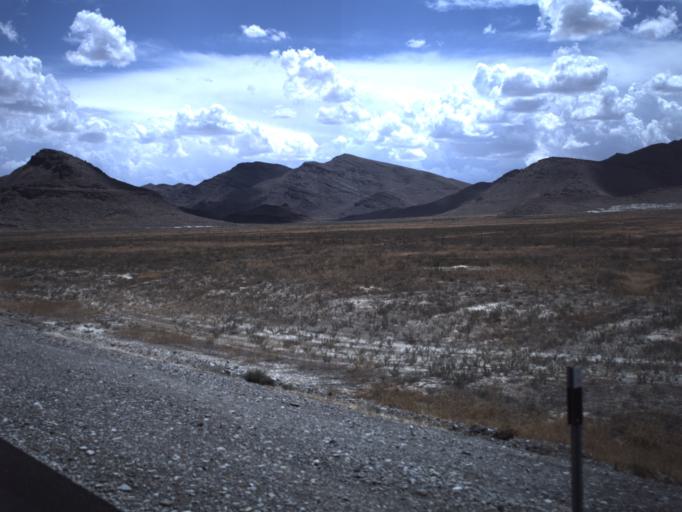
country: US
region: Utah
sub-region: Beaver County
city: Milford
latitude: 39.0709
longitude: -113.4629
